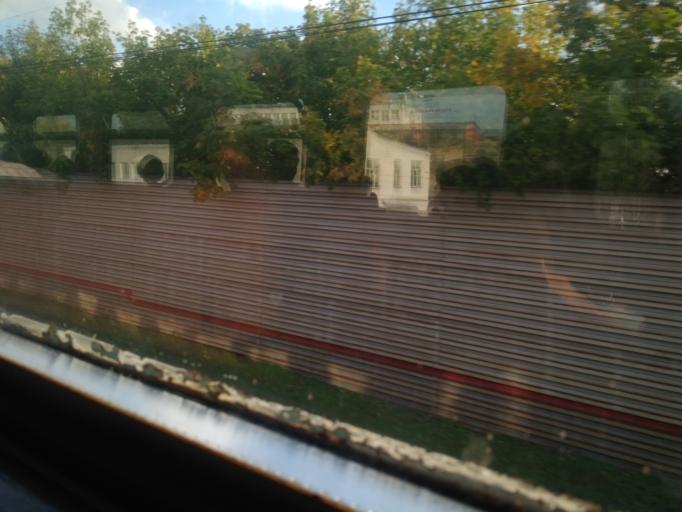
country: RU
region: Moscow
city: Ryazanskiy
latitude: 55.7395
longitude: 37.7484
